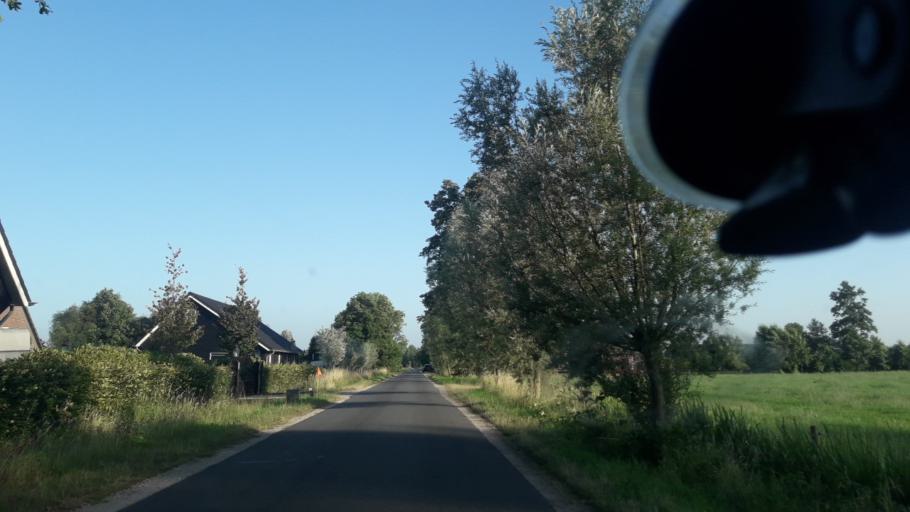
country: NL
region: Gelderland
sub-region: Gemeente Ede
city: Ede
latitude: 52.0136
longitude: 5.6133
